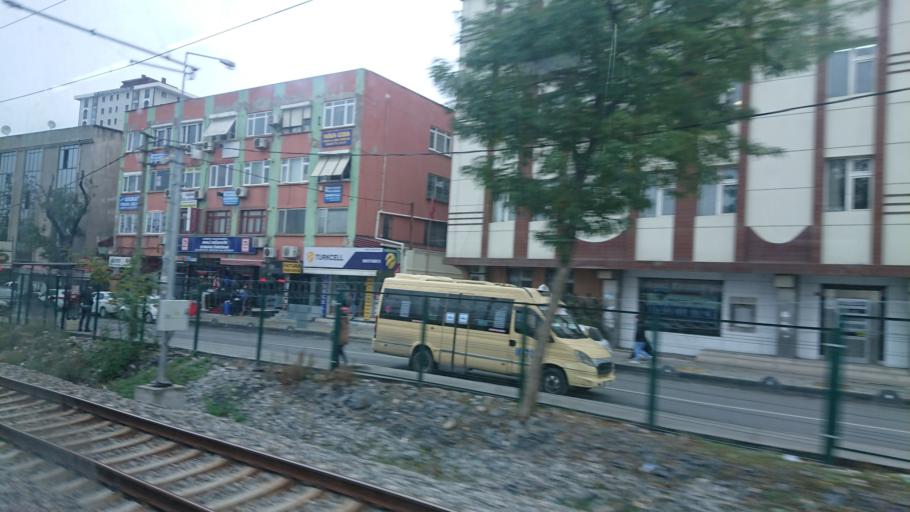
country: TR
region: Istanbul
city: Mahmutbey
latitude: 41.0091
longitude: 28.7746
